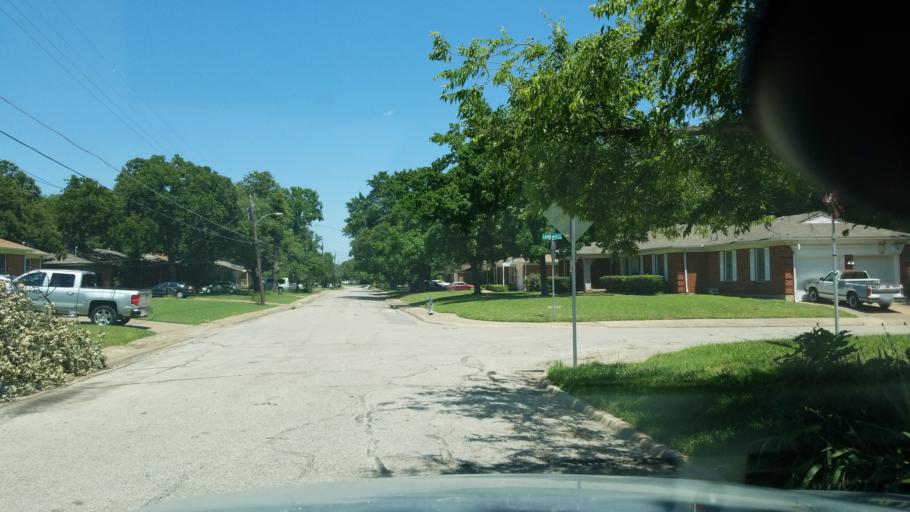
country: US
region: Texas
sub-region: Dallas County
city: Irving
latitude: 32.8285
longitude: -96.9309
